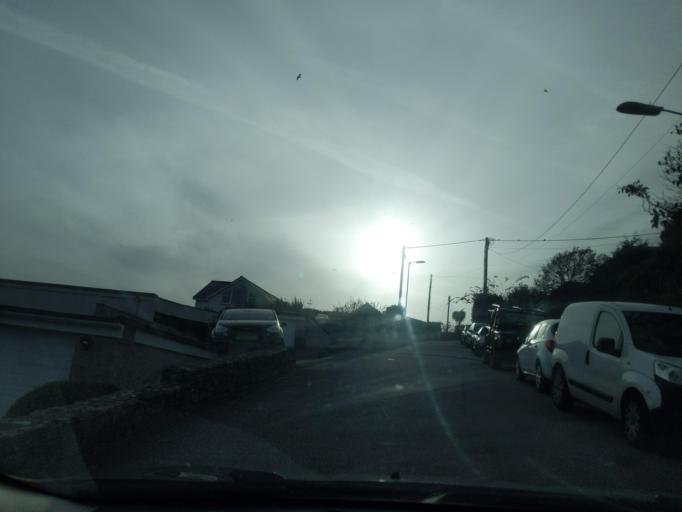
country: GB
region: England
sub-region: Cornwall
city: Looe
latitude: 50.3593
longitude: -4.4428
